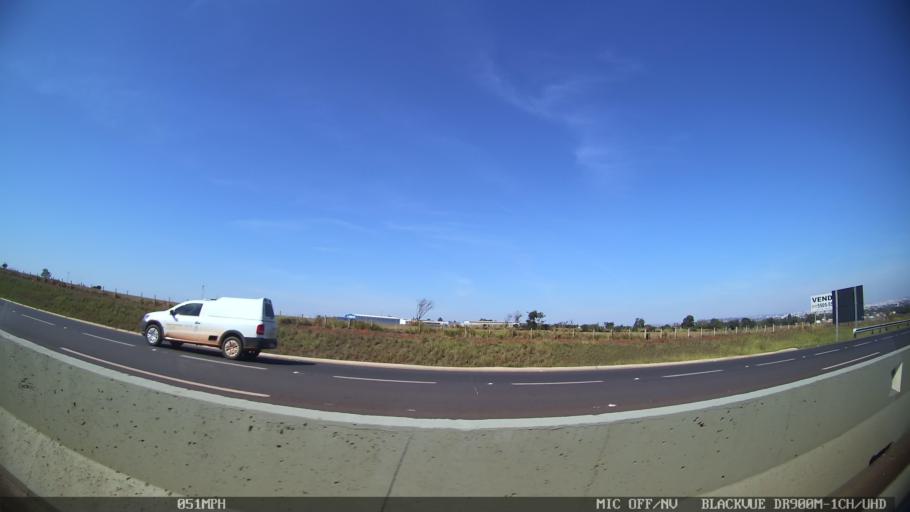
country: BR
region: Sao Paulo
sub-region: Ribeirao Preto
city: Ribeirao Preto
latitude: -21.0963
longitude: -47.7967
